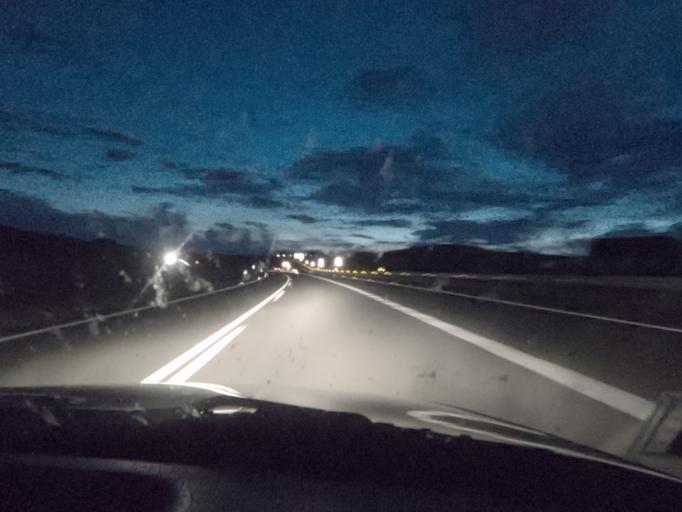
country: ES
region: Extremadura
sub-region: Provincia de Caceres
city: Galisteo
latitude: 39.9830
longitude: -6.3154
